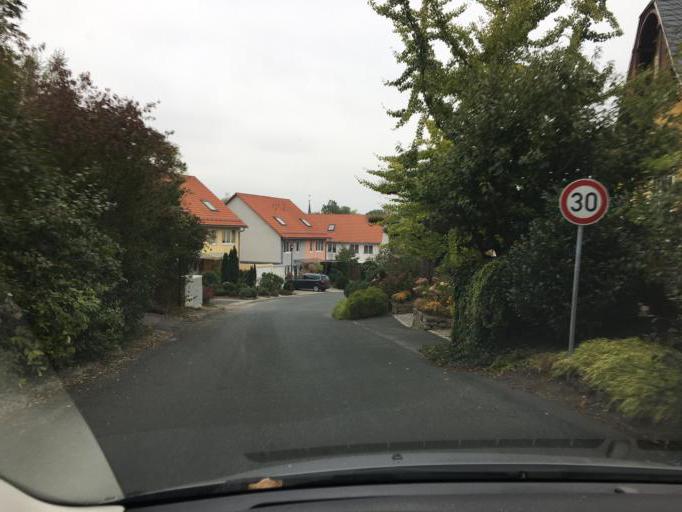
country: DE
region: Saxony
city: Freital
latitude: 51.0011
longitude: 13.6693
